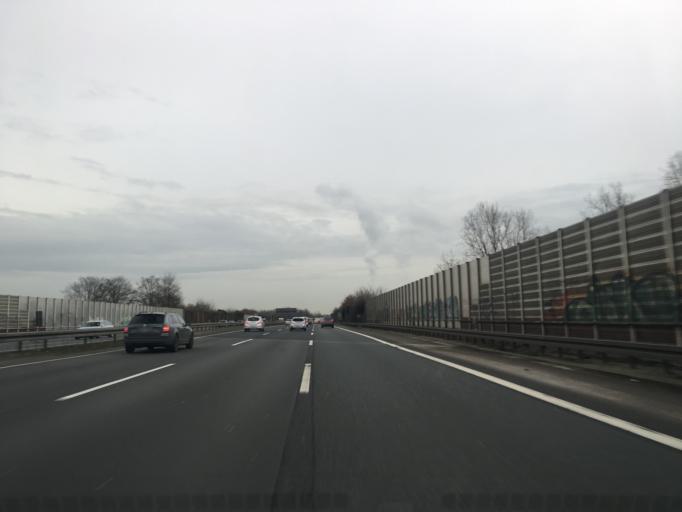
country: DE
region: North Rhine-Westphalia
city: Meiderich
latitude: 51.5115
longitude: 6.8193
